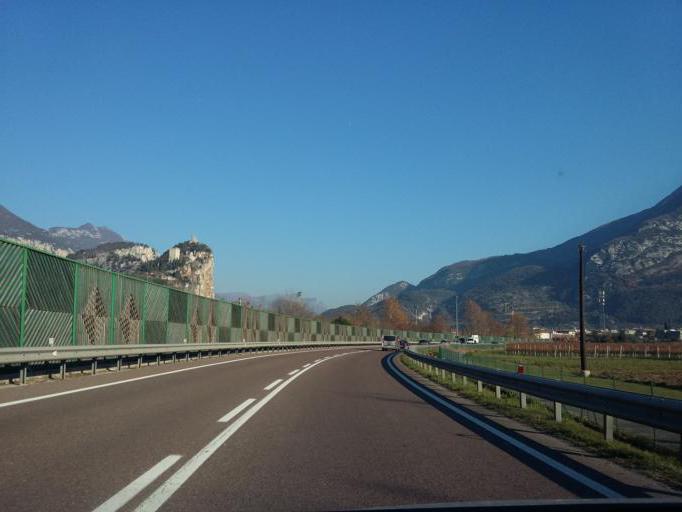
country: IT
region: Trentino-Alto Adige
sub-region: Provincia di Trento
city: Arco
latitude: 45.9114
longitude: 10.8847
